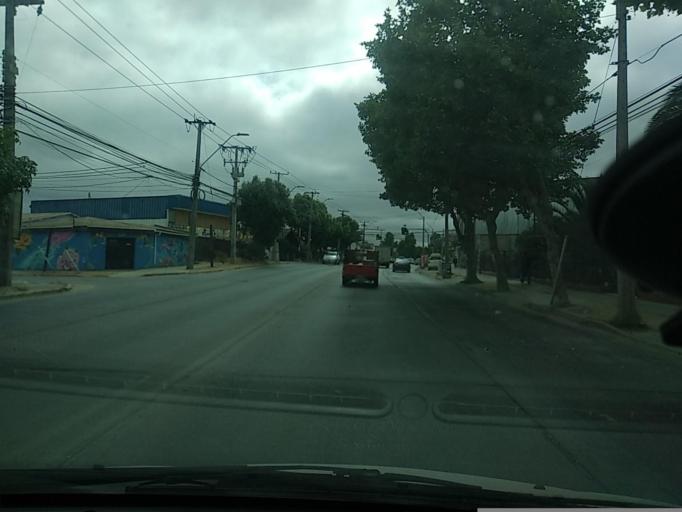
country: CL
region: Valparaiso
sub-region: Provincia de Marga Marga
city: Villa Alemana
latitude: -33.0446
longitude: -71.3849
